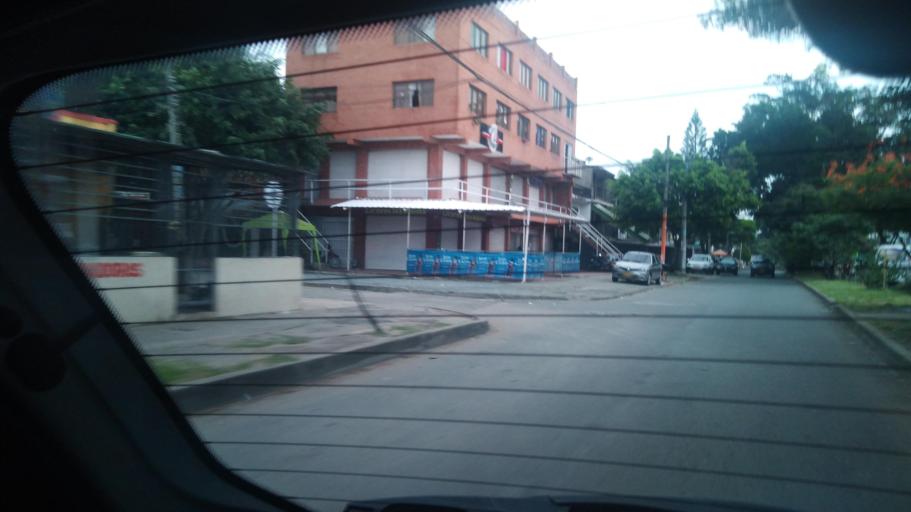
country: CO
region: Valle del Cauca
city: Cali
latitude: 3.4247
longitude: -76.5106
